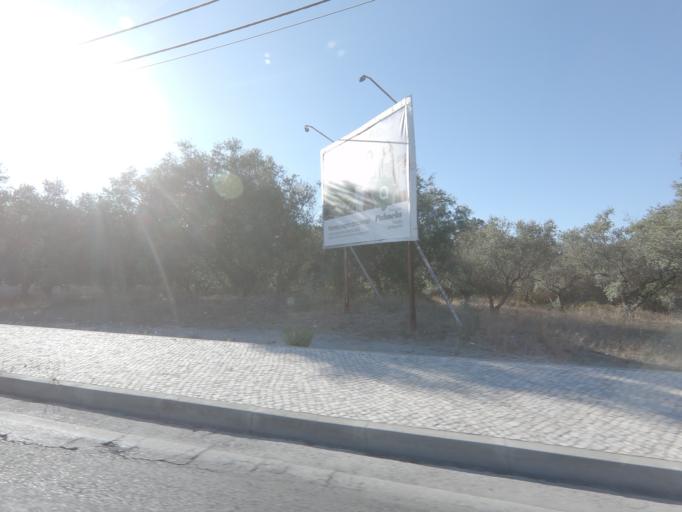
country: PT
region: Setubal
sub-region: Palmela
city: Quinta do Anjo
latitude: 38.5500
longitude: -8.9806
